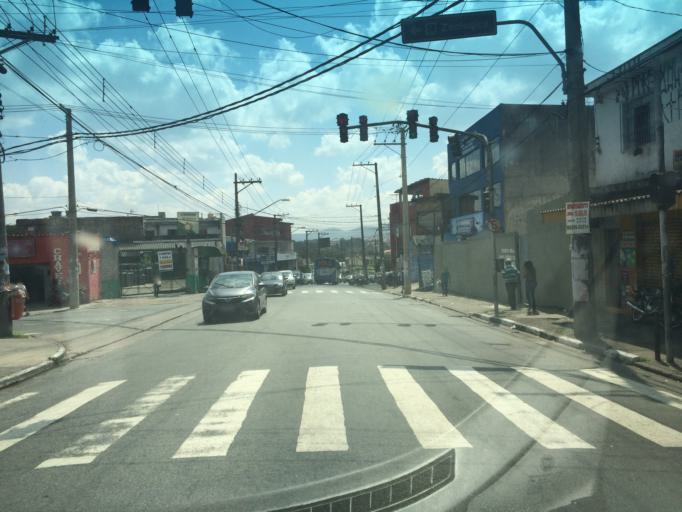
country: BR
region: Sao Paulo
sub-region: Guarulhos
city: Guarulhos
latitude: -23.4439
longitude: -46.5486
